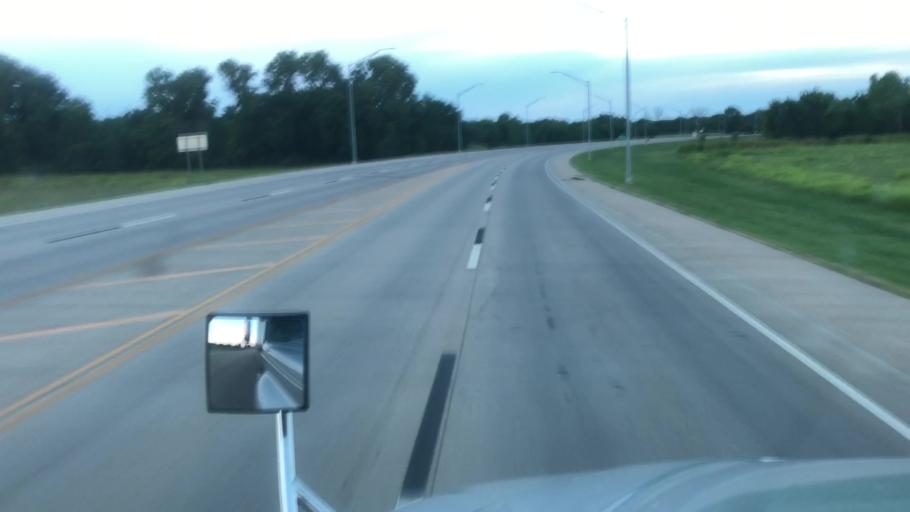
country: US
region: Oklahoma
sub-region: Kay County
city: Ponca City
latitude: 36.6829
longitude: -97.0700
